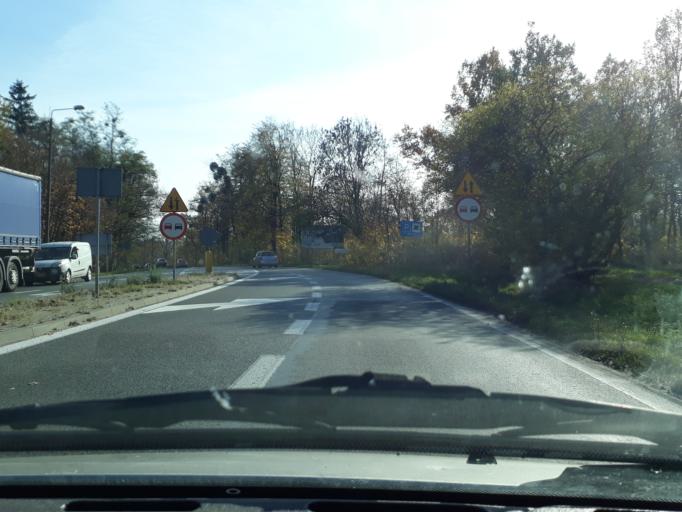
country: PL
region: Silesian Voivodeship
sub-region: Powiat tarnogorski
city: Tarnowskie Gory
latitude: 50.4417
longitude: 18.8357
